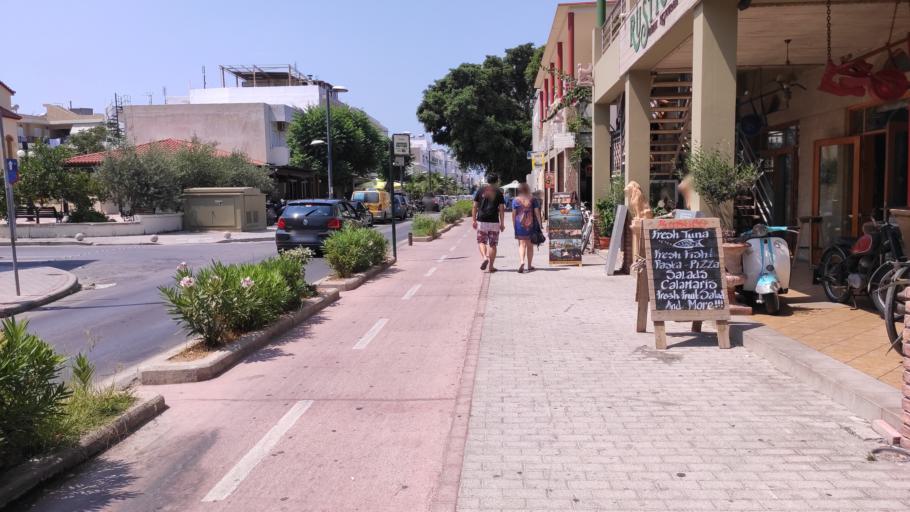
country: GR
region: South Aegean
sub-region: Nomos Dodekanisou
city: Kos
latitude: 36.8990
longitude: 27.2860
